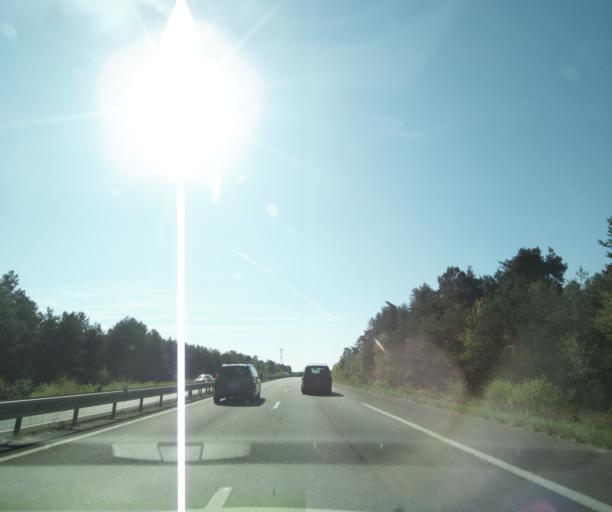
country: FR
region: Centre
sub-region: Departement du Loir-et-Cher
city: Lamotte-Beuvron
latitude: 47.5922
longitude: 1.9866
